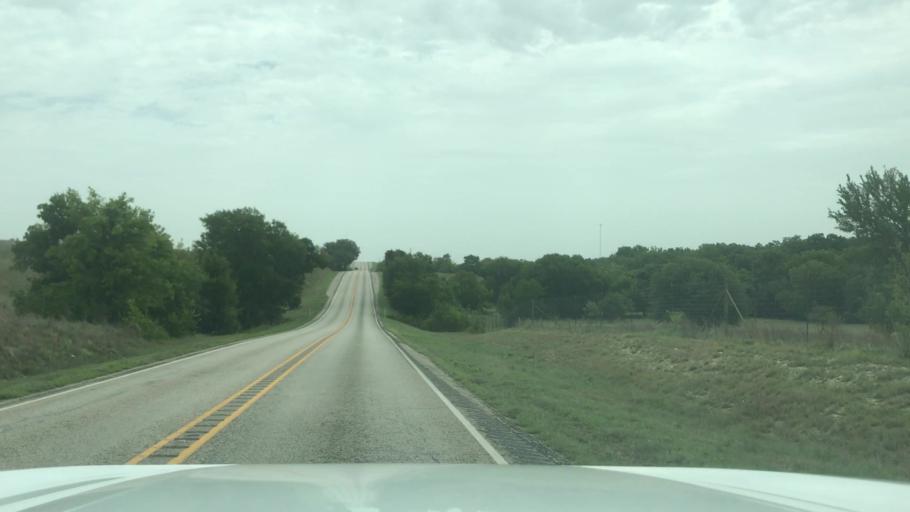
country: US
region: Texas
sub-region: Hamilton County
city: Hico
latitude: 32.0554
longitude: -98.1797
